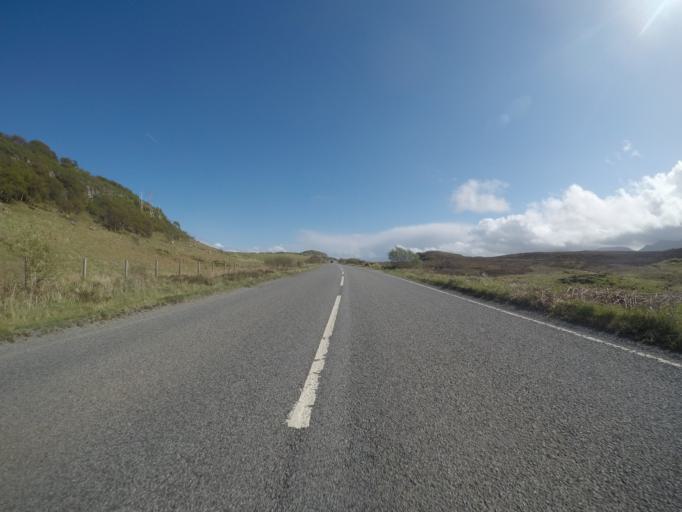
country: GB
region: Scotland
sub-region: Highland
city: Portree
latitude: 57.6044
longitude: -6.1701
